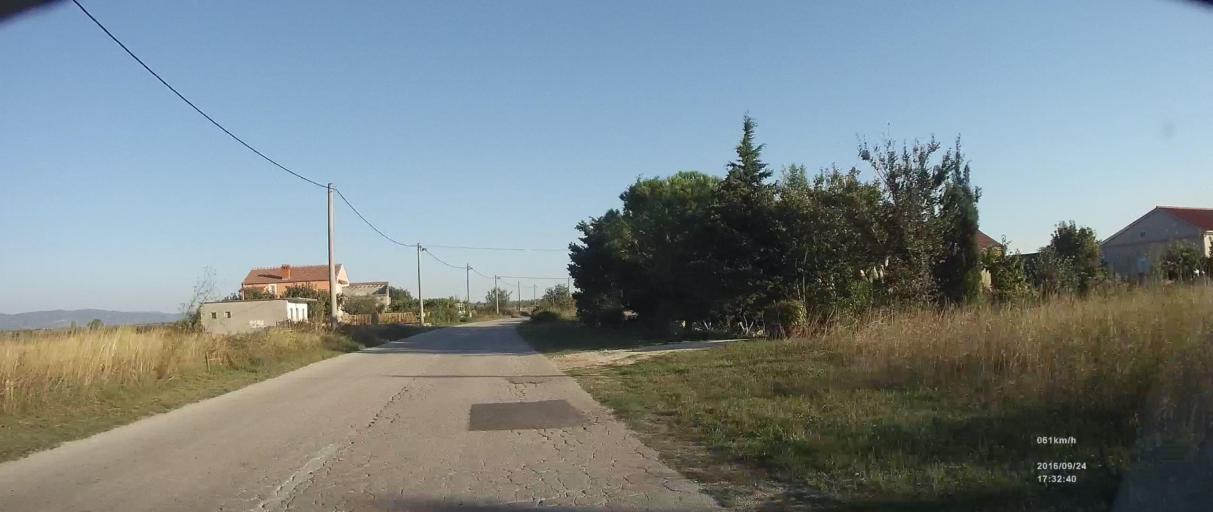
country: HR
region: Zadarska
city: Posedarje
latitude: 44.1806
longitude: 15.4521
